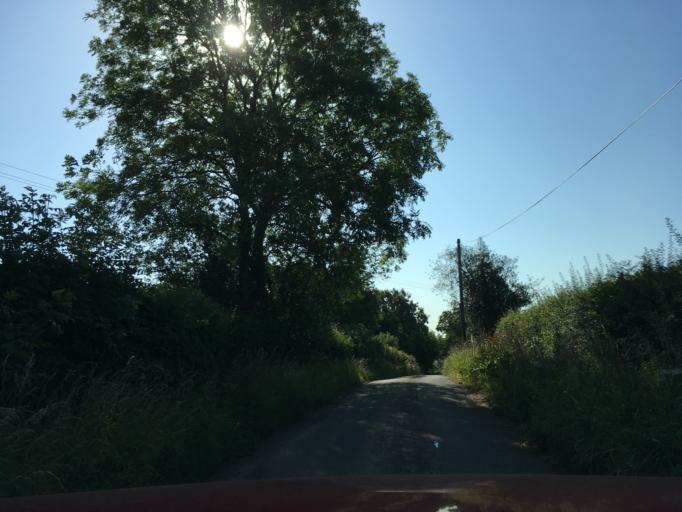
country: GB
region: England
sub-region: Gloucestershire
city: Lydney
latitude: 51.7524
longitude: -2.4699
